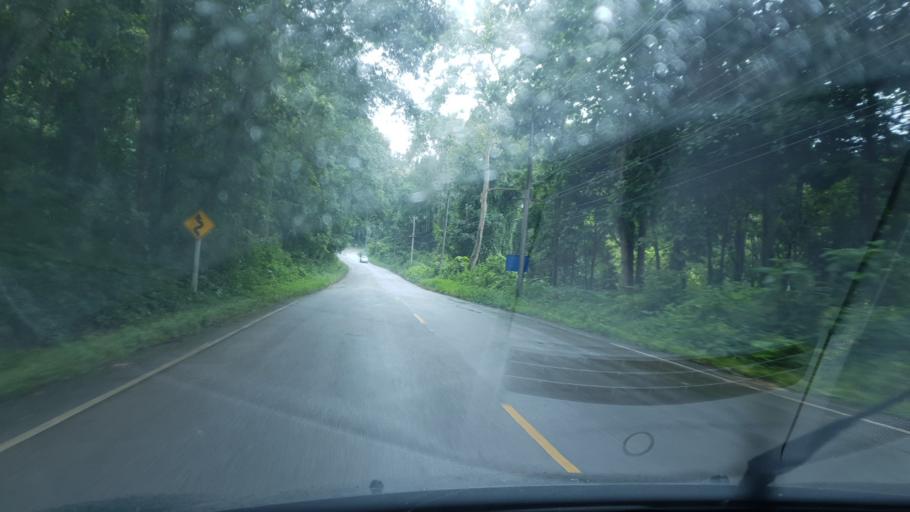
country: TH
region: Mae Hong Son
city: Mae La Noi
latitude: 18.2872
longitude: 97.9362
